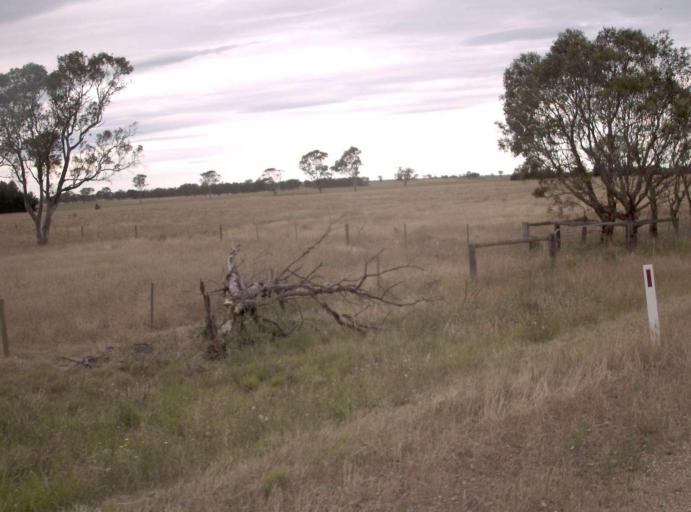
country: AU
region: Victoria
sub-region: Wellington
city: Sale
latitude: -37.9950
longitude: 147.3404
